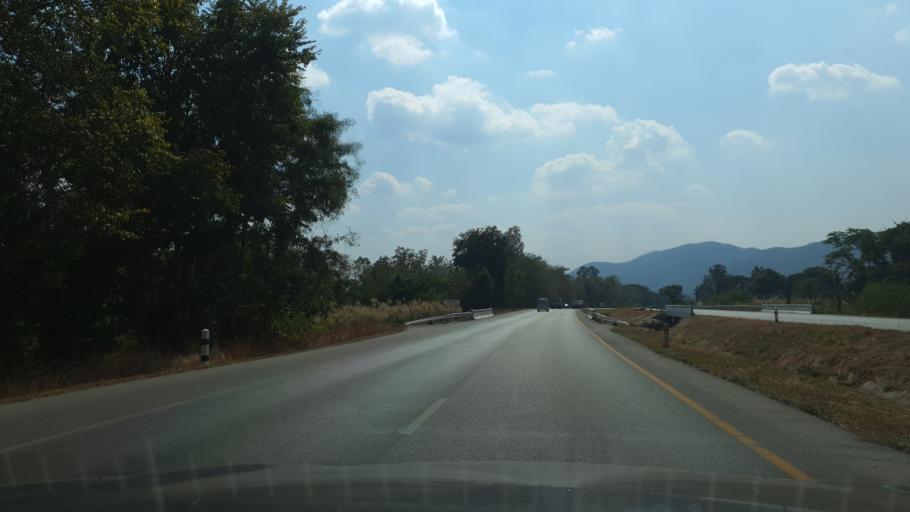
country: TH
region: Lampang
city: Mae Phrik
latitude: 17.3761
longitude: 99.1492
